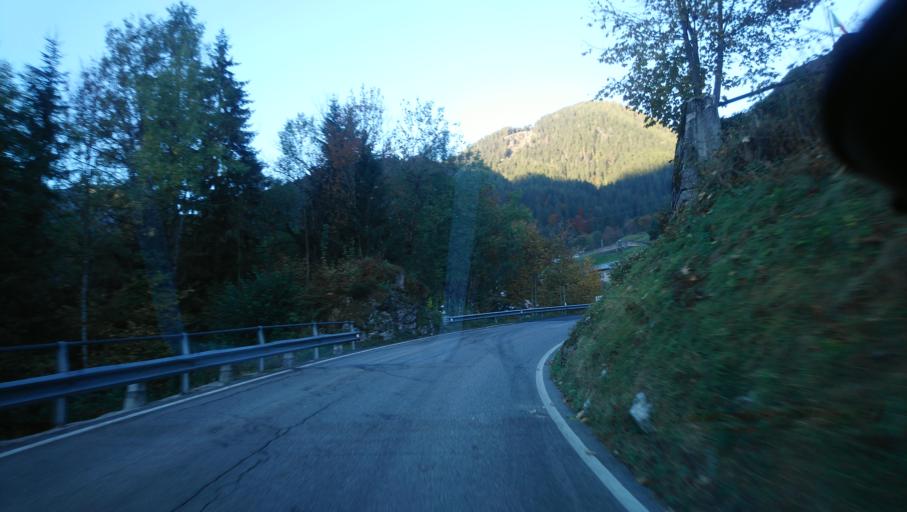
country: IT
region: Veneto
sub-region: Provincia di Belluno
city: Falcade Alto
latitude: 46.3535
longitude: 11.8625
